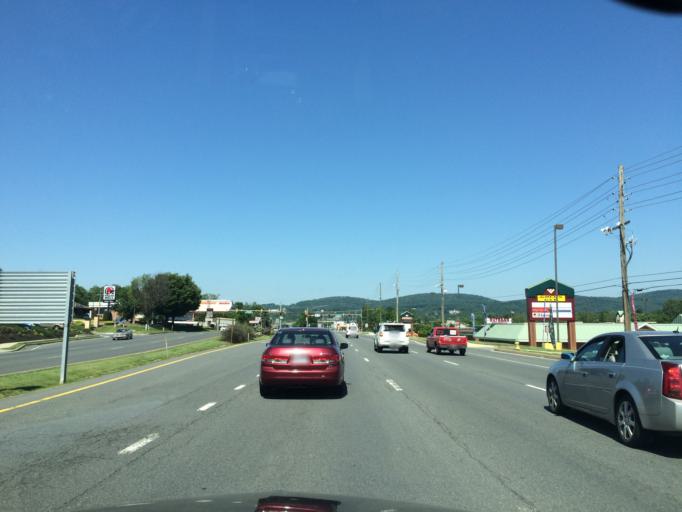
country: US
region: Maryland
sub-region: Frederick County
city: Frederick
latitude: 39.4173
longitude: -77.4436
